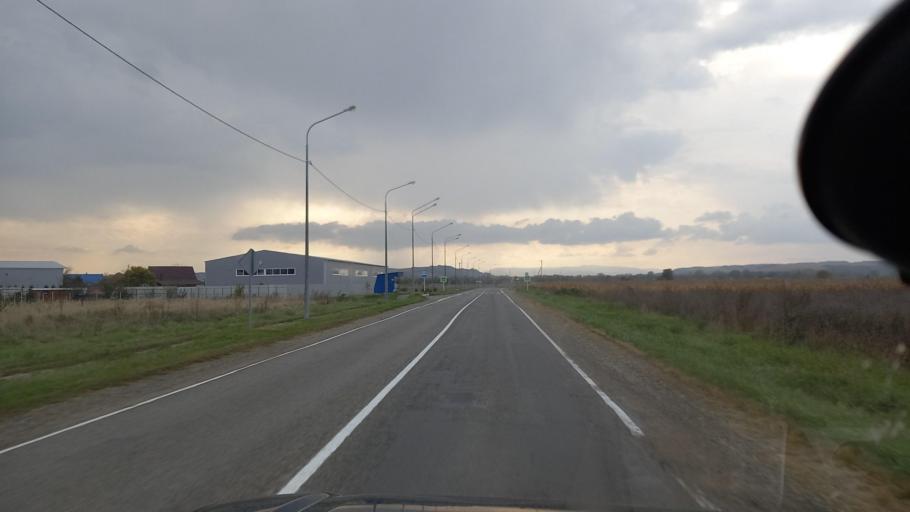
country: RU
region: Krasnodarskiy
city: Mostovskoy
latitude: 44.3945
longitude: 40.7690
